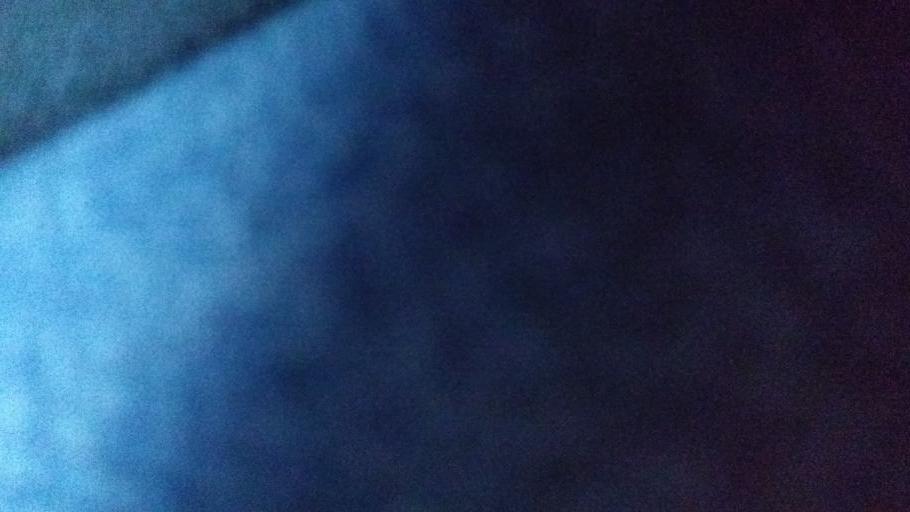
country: MX
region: Yucatan
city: Itzincab Palomeque
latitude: 20.9289
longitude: -89.6660
